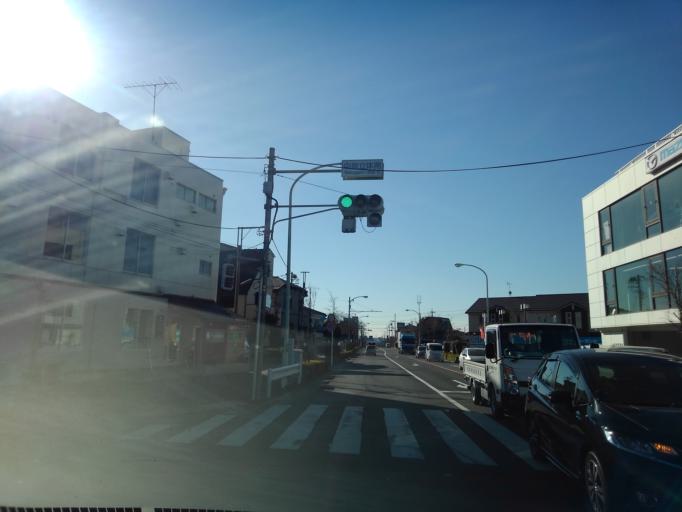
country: JP
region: Tokyo
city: Hino
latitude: 35.7067
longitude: 139.3780
